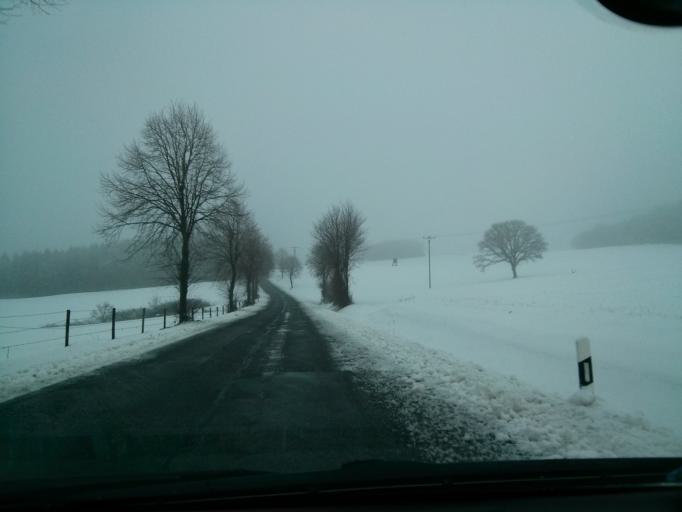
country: DE
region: Rheinland-Pfalz
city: Kirchsahr
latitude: 50.5070
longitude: 6.8444
